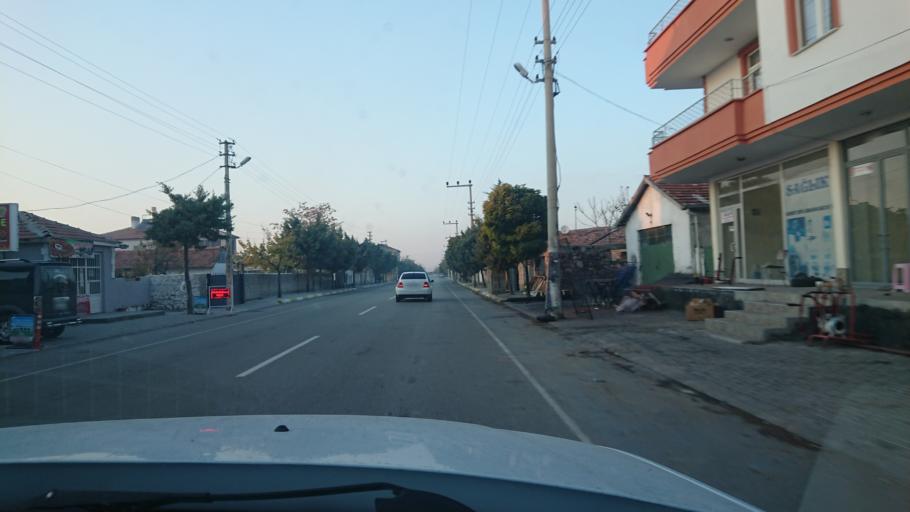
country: TR
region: Aksaray
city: Aksaray
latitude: 38.3033
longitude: 34.0696
